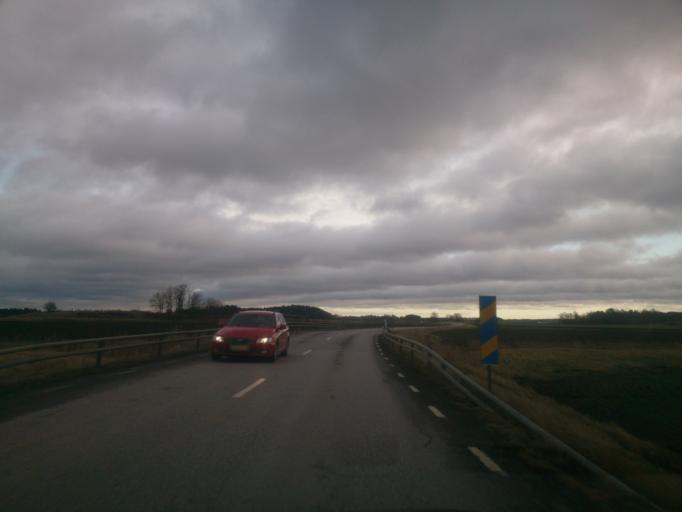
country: SE
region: OEstergoetland
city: Lindo
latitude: 58.5807
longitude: 16.3341
